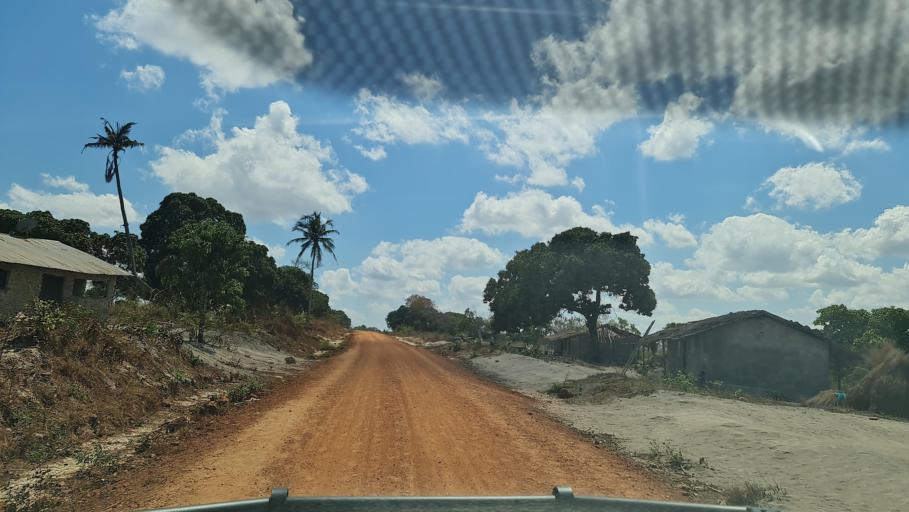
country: MZ
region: Nampula
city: Nacala
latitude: -14.1719
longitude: 40.2444
